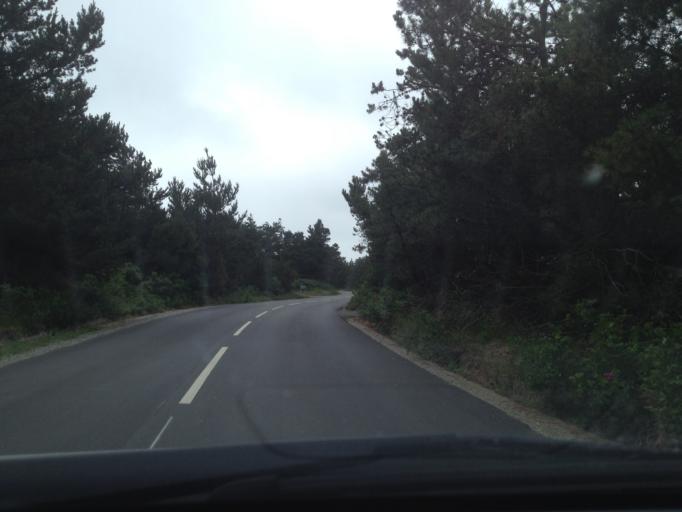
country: DK
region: South Denmark
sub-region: Varde Kommune
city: Oksbol
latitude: 55.5511
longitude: 8.1567
